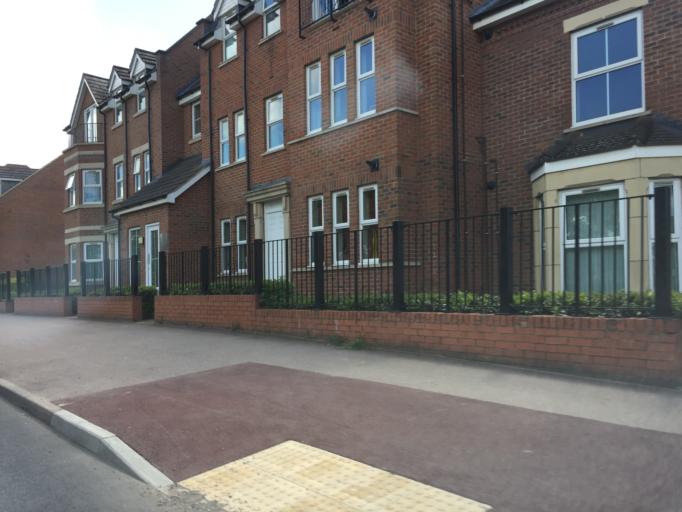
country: GB
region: England
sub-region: Milton Keynes
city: Woburn Sands
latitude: 52.0175
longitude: -0.6521
